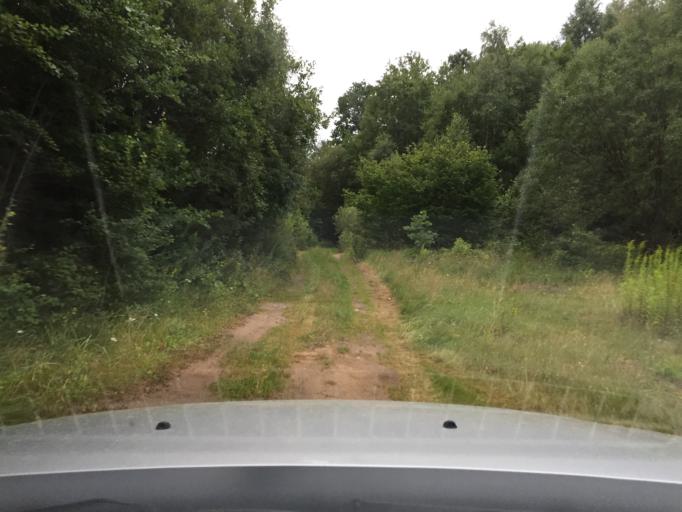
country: SE
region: Skane
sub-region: Hassleholms Kommun
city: Sosdala
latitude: 56.0432
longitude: 13.6982
